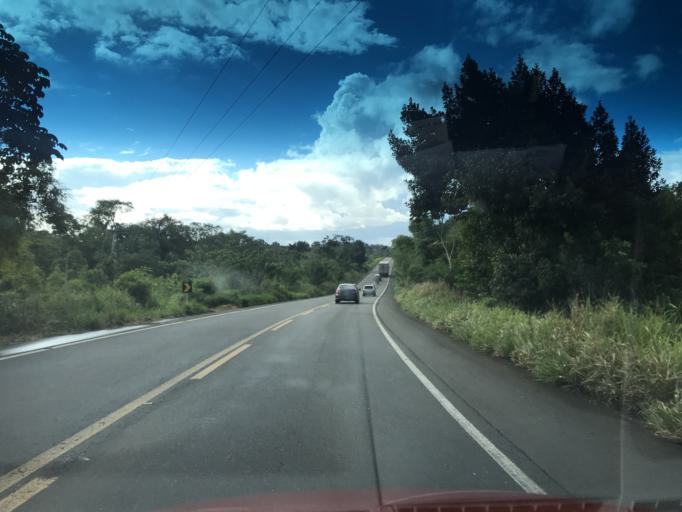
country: BR
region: Bahia
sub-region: Ibirapitanga
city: Ibirapitanga
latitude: -14.1687
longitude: -39.3279
